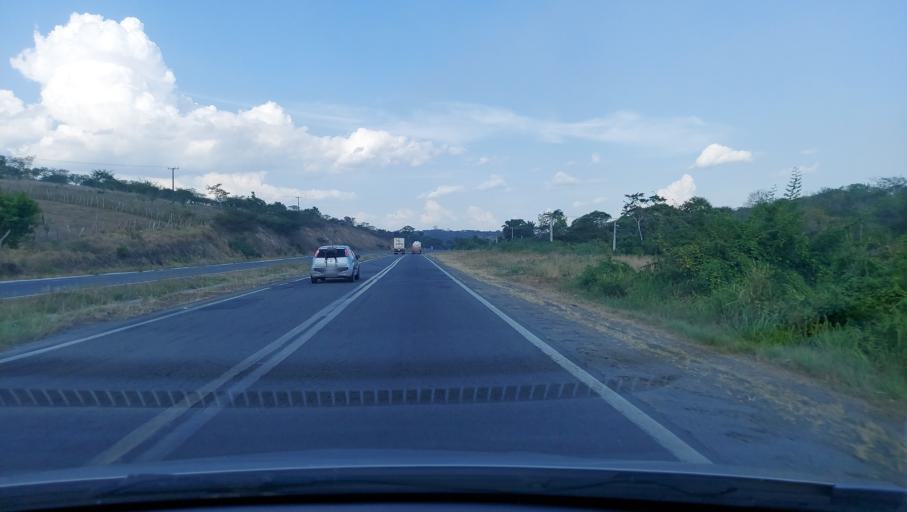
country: BR
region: Bahia
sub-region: Santo Estevao
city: Santo Estevao
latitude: -12.3952
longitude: -39.1582
